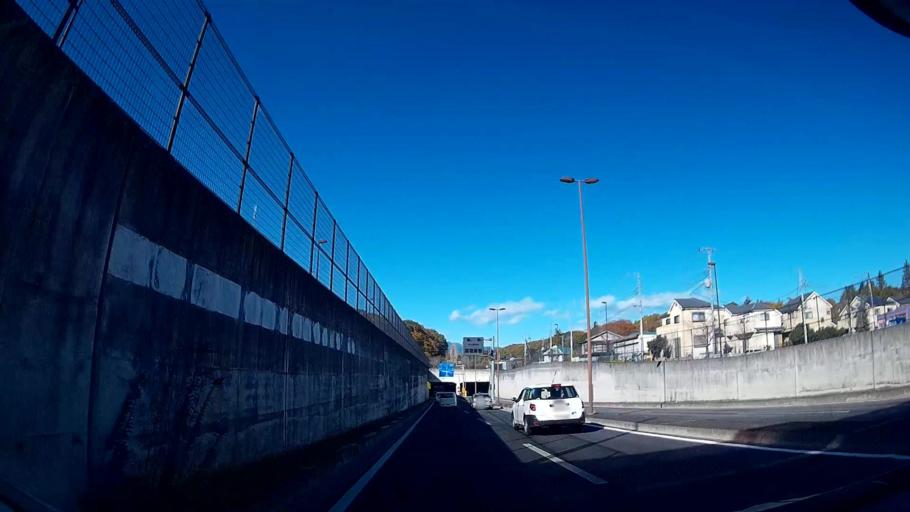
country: JP
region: Tokyo
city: Fussa
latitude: 35.7084
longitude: 139.2908
